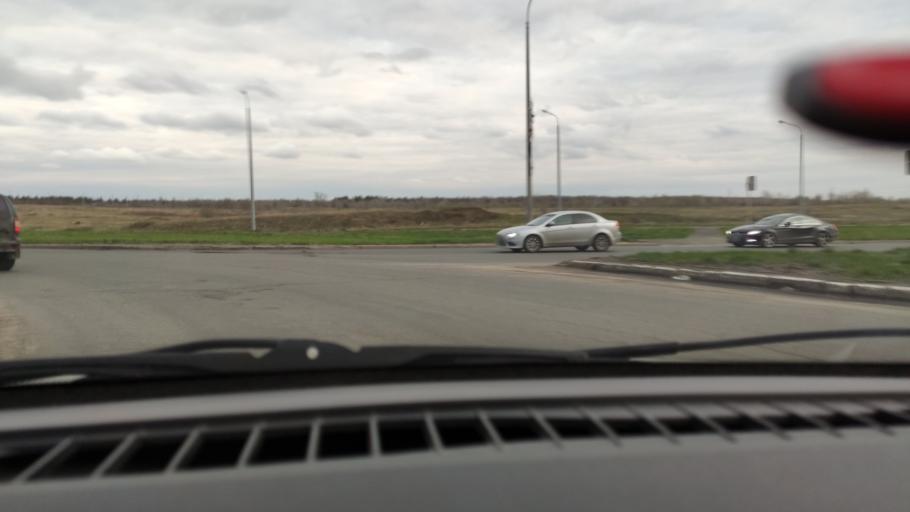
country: RU
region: Orenburg
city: Orenburg
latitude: 51.8101
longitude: 55.1794
